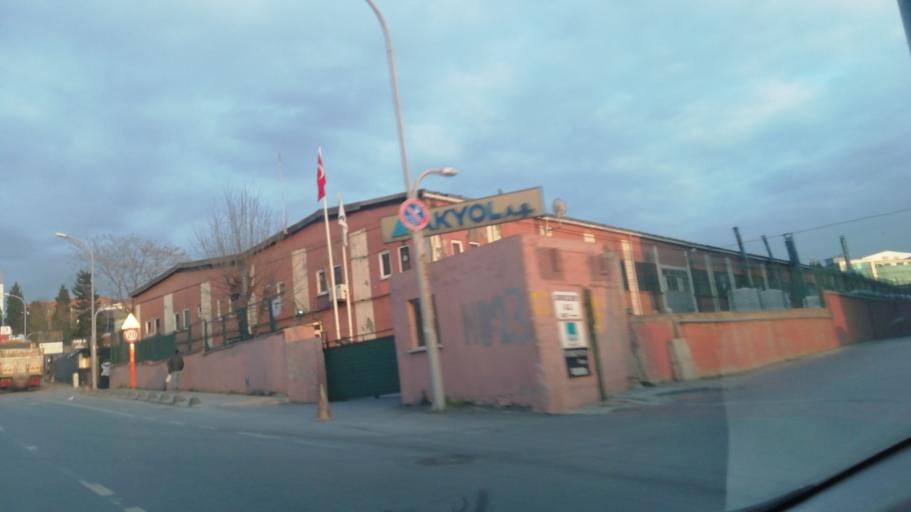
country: TR
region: Istanbul
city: Mahmutbey
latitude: 41.0315
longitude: 28.8215
